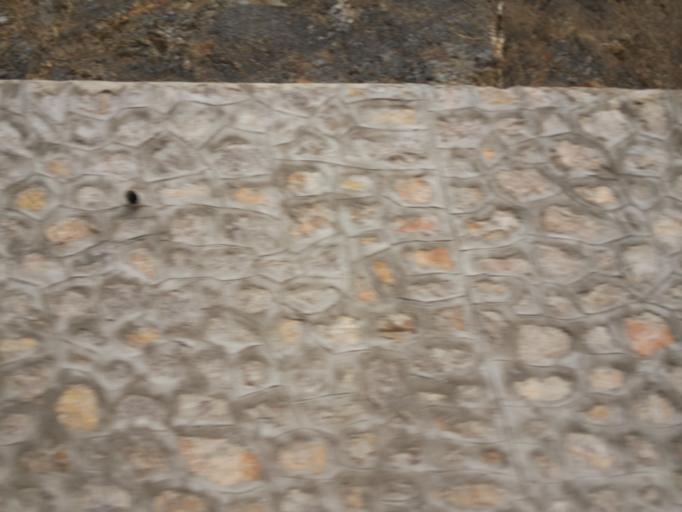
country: TR
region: Sinop
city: Duragan
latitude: 41.4640
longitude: 35.0459
